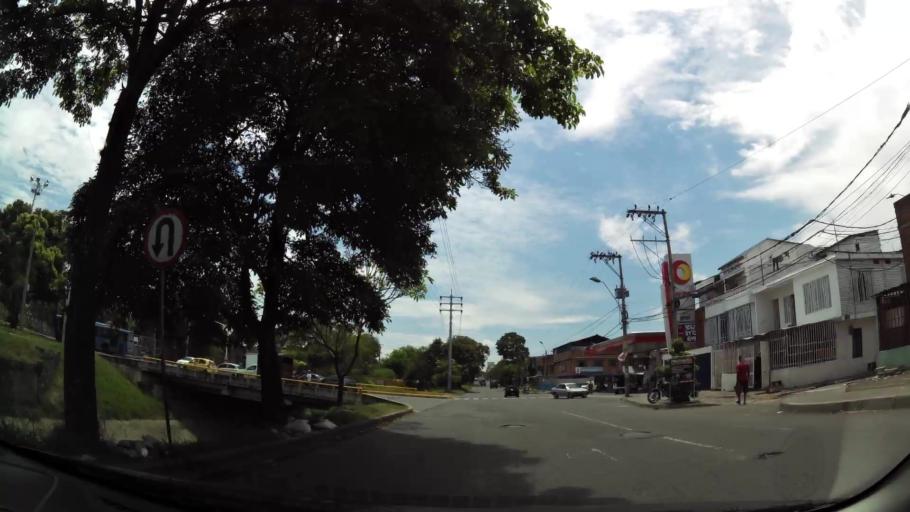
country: CO
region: Valle del Cauca
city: Cali
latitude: 3.4436
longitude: -76.4843
